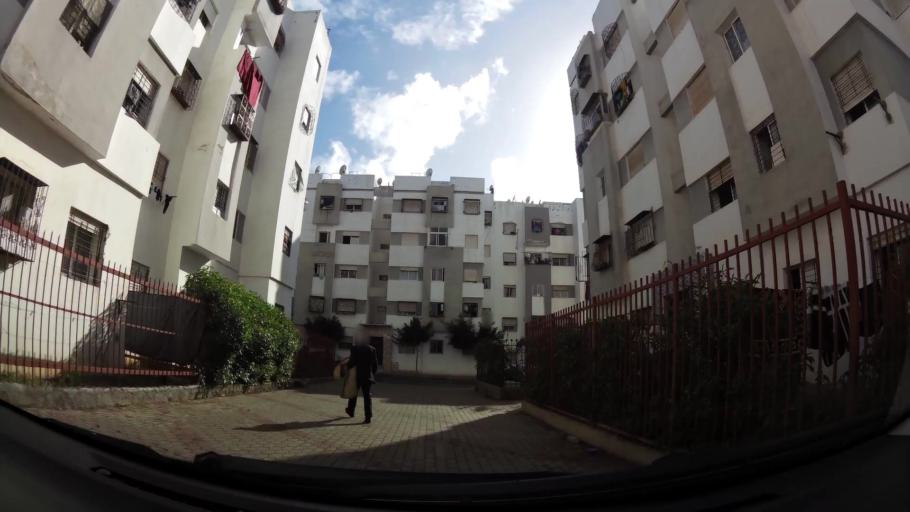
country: MA
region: Grand Casablanca
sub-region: Casablanca
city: Casablanca
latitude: 33.5564
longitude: -7.6995
